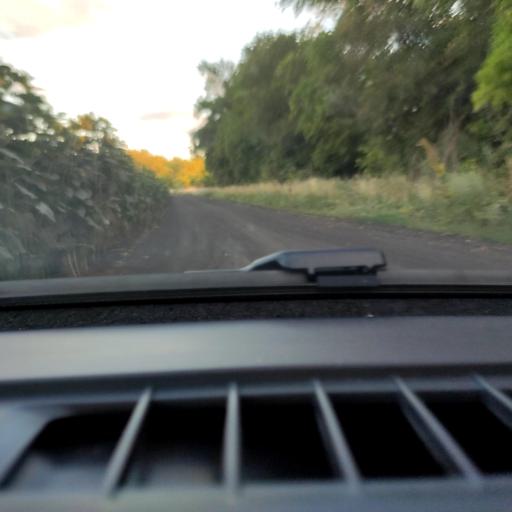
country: RU
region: Voronezj
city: Verkhnyaya Khava
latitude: 51.5959
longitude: 39.8415
